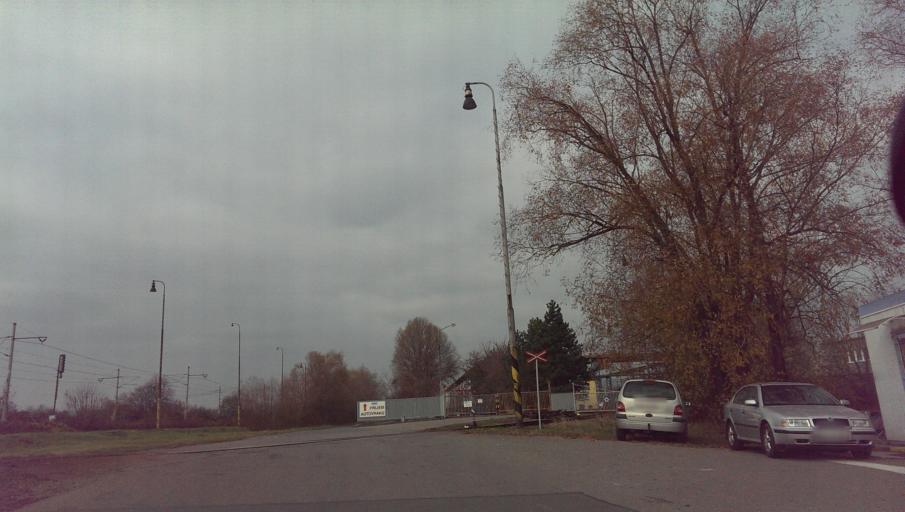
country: CZ
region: Zlin
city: Tlumacov
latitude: 49.2614
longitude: 17.4970
